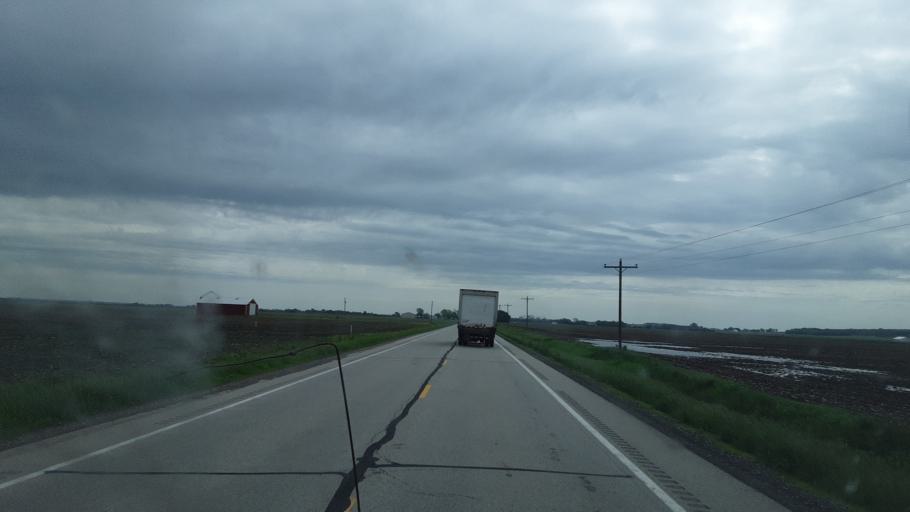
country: US
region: Illinois
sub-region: Mason County
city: Mason City
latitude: 40.3046
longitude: -89.7119
